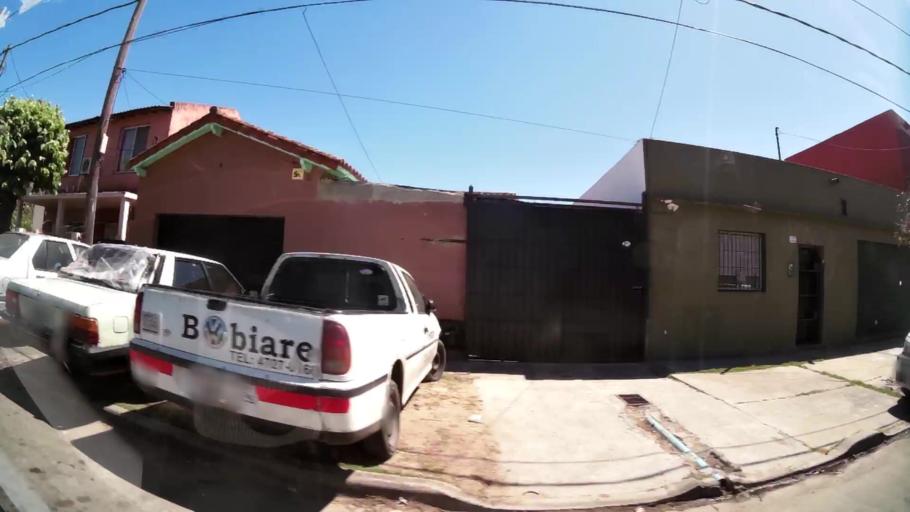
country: AR
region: Buenos Aires
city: Hurlingham
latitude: -34.5031
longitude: -58.6326
